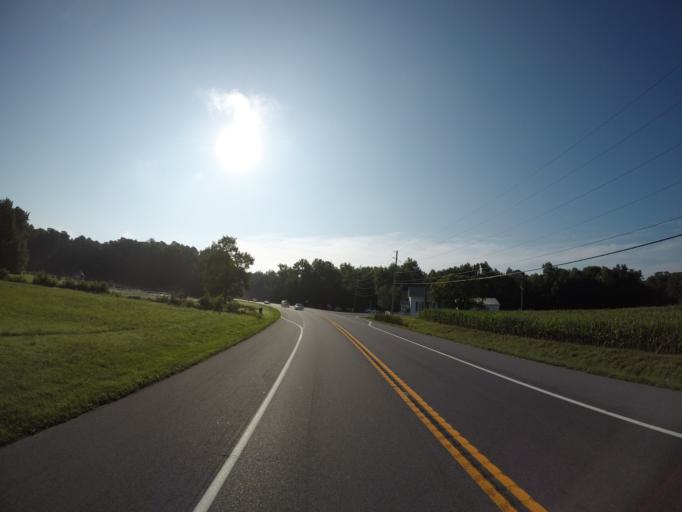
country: US
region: Delaware
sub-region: Sussex County
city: Georgetown
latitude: 38.6926
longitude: -75.4813
